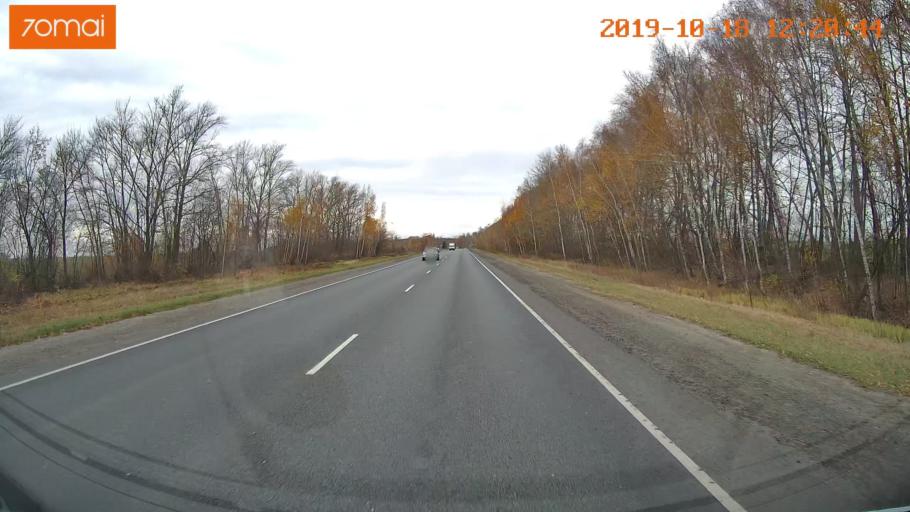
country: RU
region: Rjazan
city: Bagramovo
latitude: 54.5023
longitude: 39.4839
